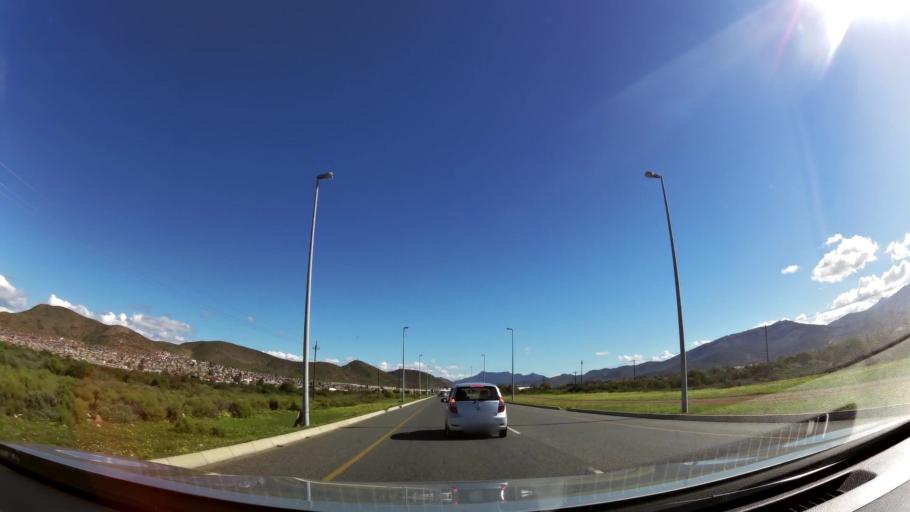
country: ZA
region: Western Cape
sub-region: Cape Winelands District Municipality
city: Ashton
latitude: -33.8148
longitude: 19.9030
